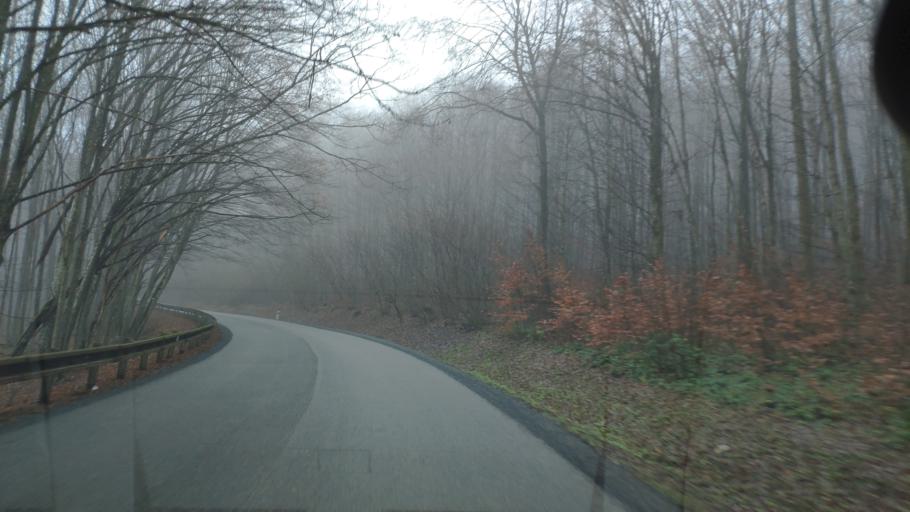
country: SK
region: Banskobystricky
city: Revuca
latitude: 48.6244
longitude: 20.2773
